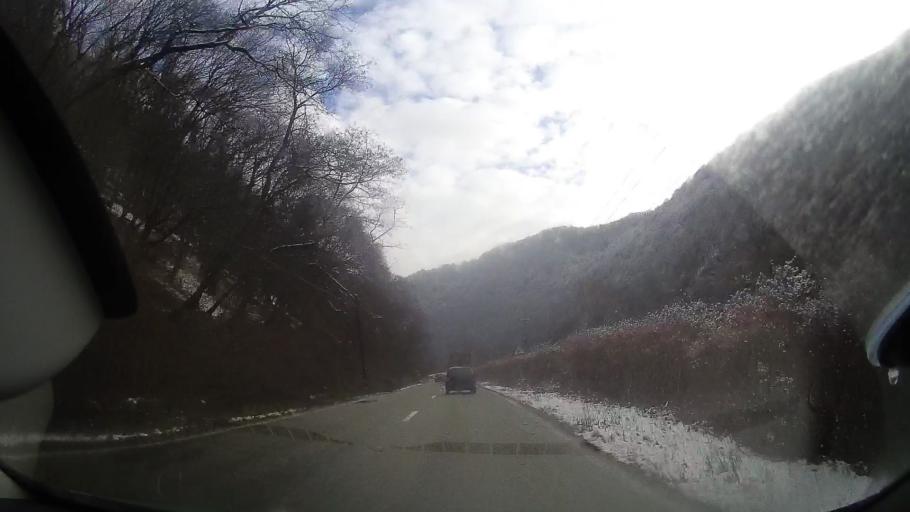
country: RO
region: Alba
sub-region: Oras Baia de Aries
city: Baia de Aries
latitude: 46.4028
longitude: 23.3447
